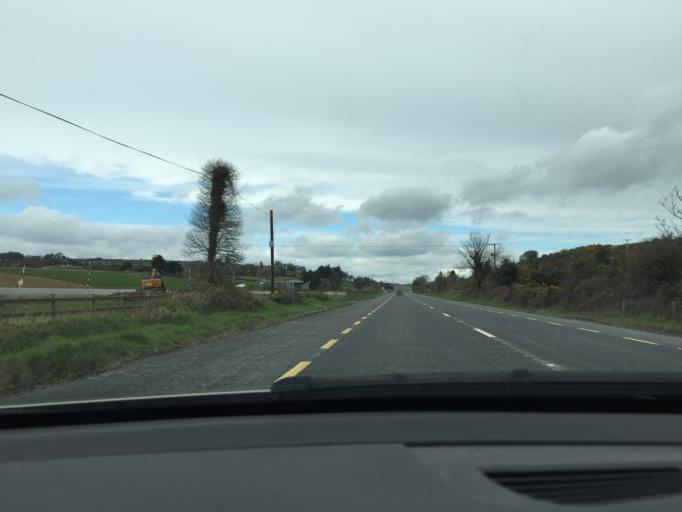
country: IE
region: Leinster
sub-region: Wicklow
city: Wicklow
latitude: 52.8900
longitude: -6.0986
